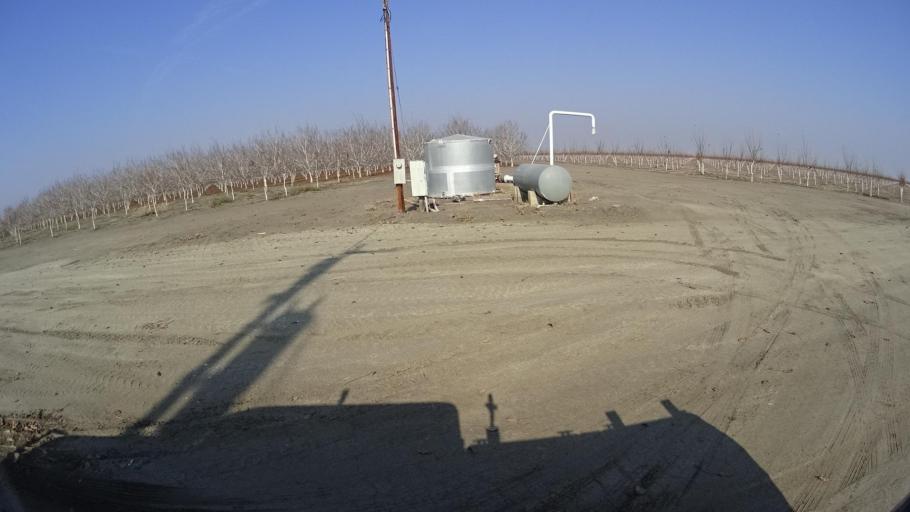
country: US
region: California
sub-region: Kern County
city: Buttonwillow
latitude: 35.3694
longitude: -119.4139
